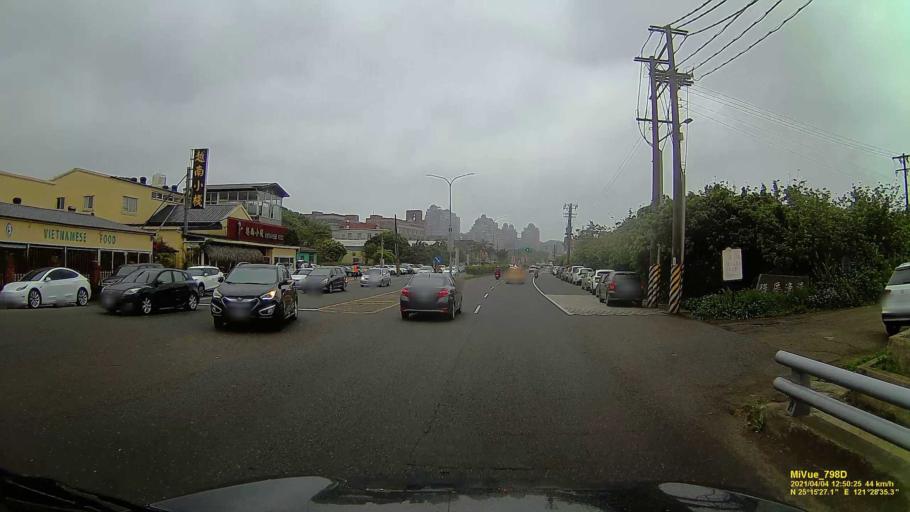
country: TW
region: Taipei
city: Taipei
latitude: 25.2574
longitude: 121.4764
